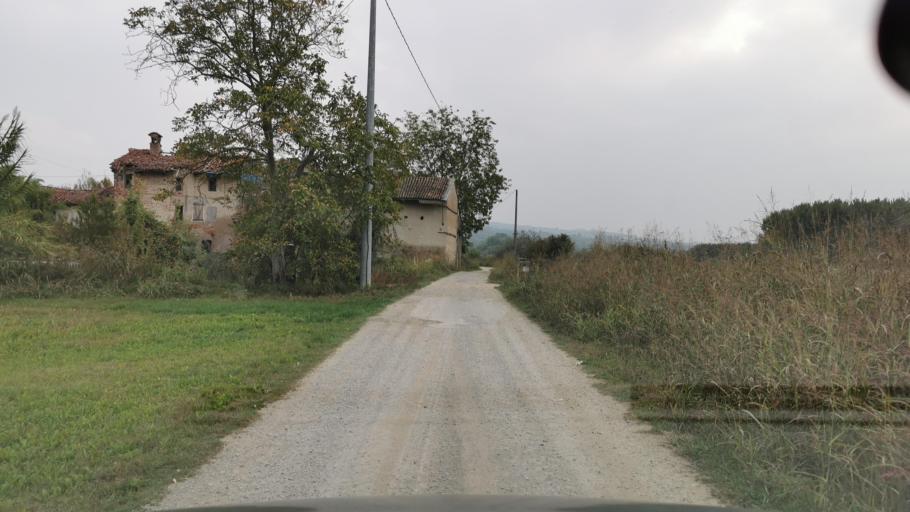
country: IT
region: Piedmont
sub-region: Provincia di Cuneo
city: Cinzano
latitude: 44.6916
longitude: 7.9125
